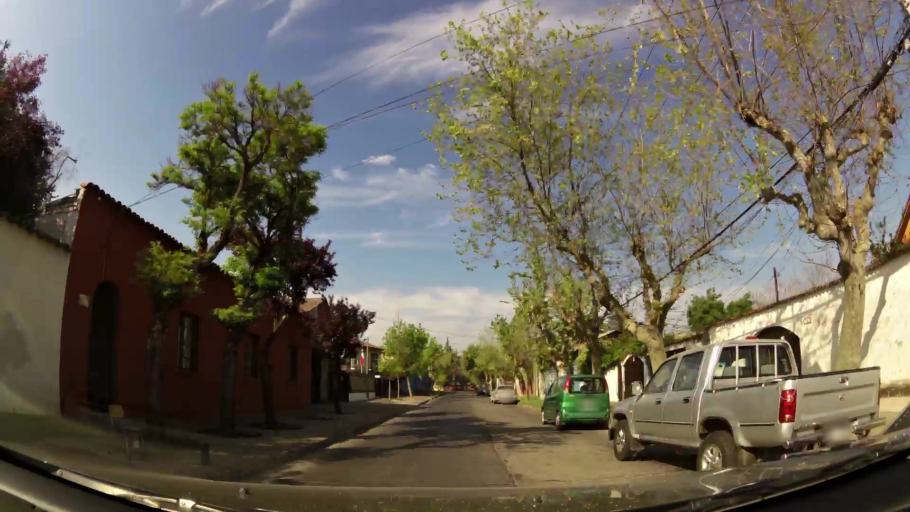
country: CL
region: Santiago Metropolitan
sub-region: Provincia de Maipo
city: San Bernardo
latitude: -33.5971
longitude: -70.7084
